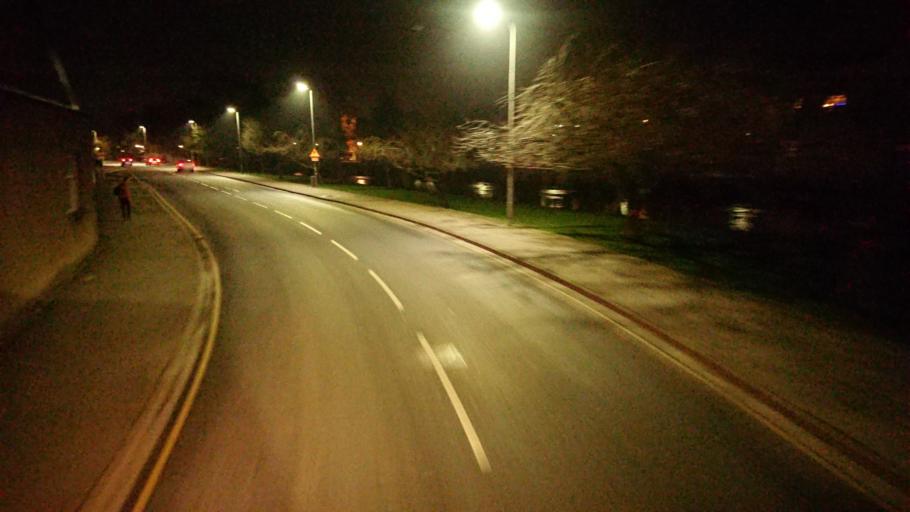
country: GB
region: England
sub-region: Cumbria
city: Kendal
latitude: 54.3260
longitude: -2.7442
